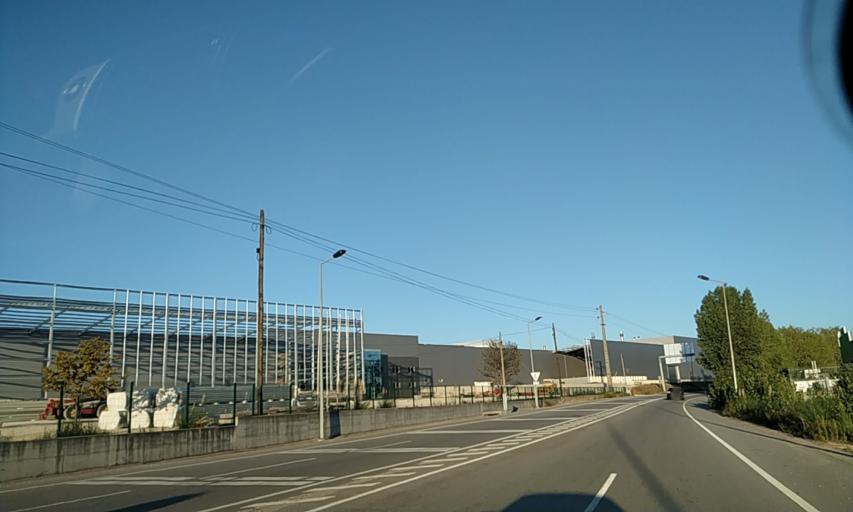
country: PT
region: Aveiro
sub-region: Oliveira do Bairro
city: Oia
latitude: 40.5563
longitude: -8.5543
